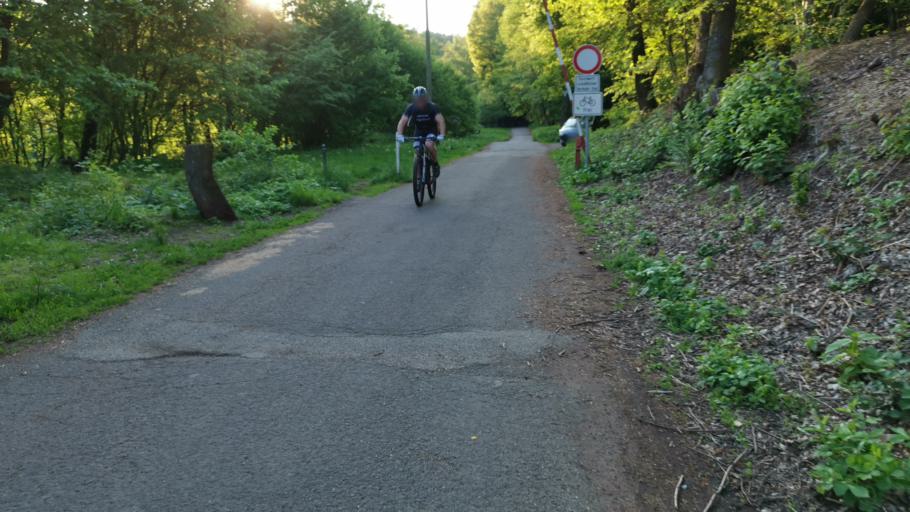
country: DE
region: Saarland
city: Kirkel
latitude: 49.2476
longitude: 7.1888
